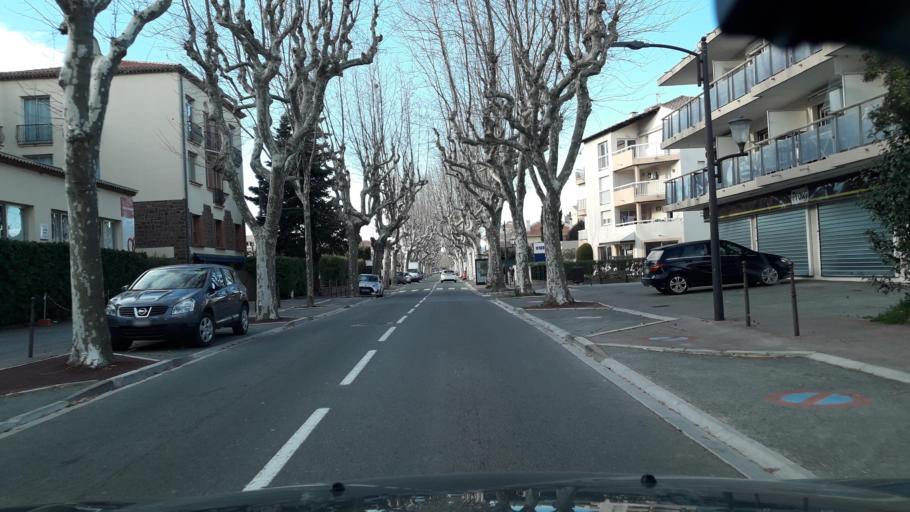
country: FR
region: Provence-Alpes-Cote d'Azur
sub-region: Departement du Var
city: Frejus
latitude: 43.4202
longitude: 6.7448
